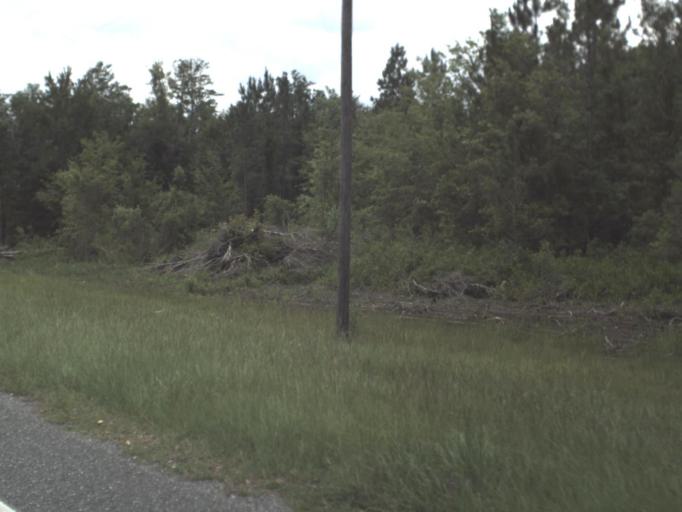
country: US
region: Florida
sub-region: Bradford County
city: Starke
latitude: 29.9686
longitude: -82.2027
